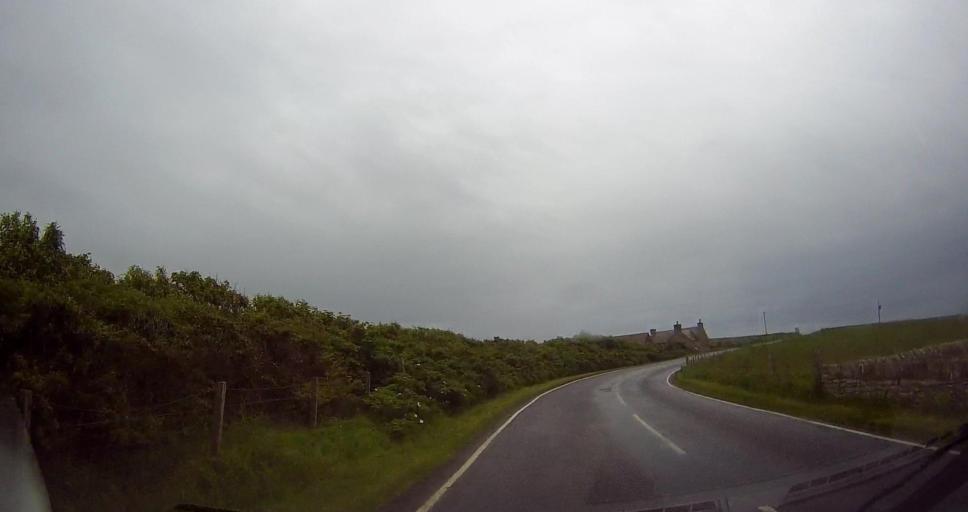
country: GB
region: Scotland
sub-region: Orkney Islands
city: Stromness
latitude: 59.0334
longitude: -3.2840
